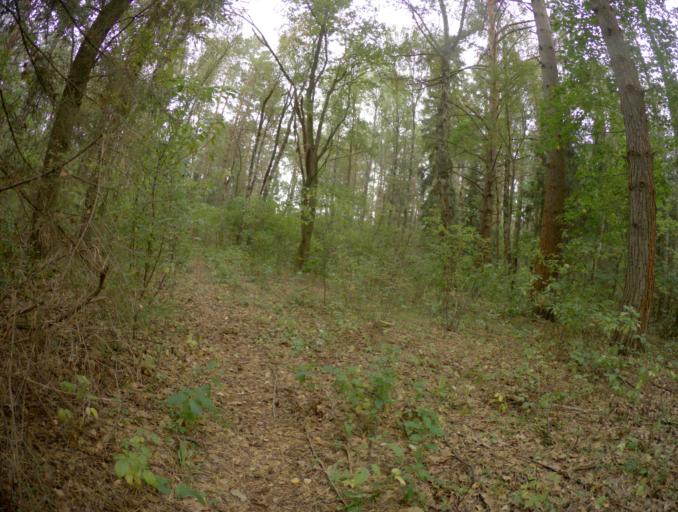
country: RU
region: Vladimir
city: Bogolyubovo
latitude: 56.1395
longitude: 40.5303
